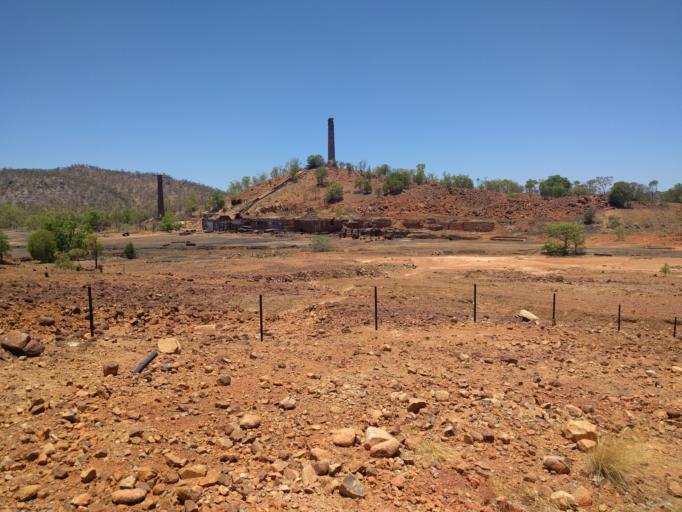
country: AU
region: Queensland
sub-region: Tablelands
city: Mareeba
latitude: -17.1525
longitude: 144.5169
